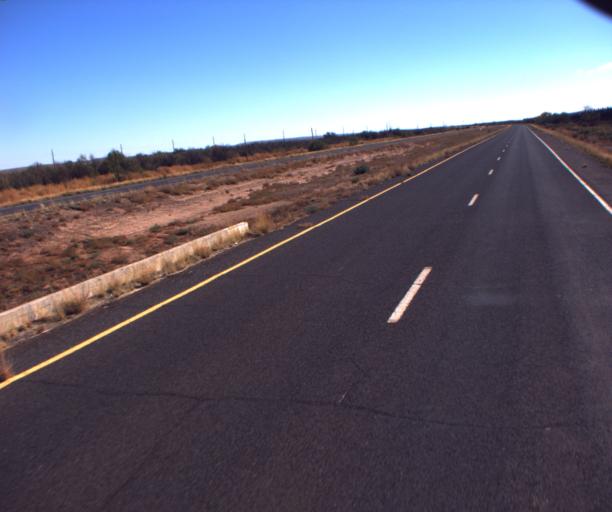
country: US
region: Arizona
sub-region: Navajo County
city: Winslow
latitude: 35.0103
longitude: -110.6675
